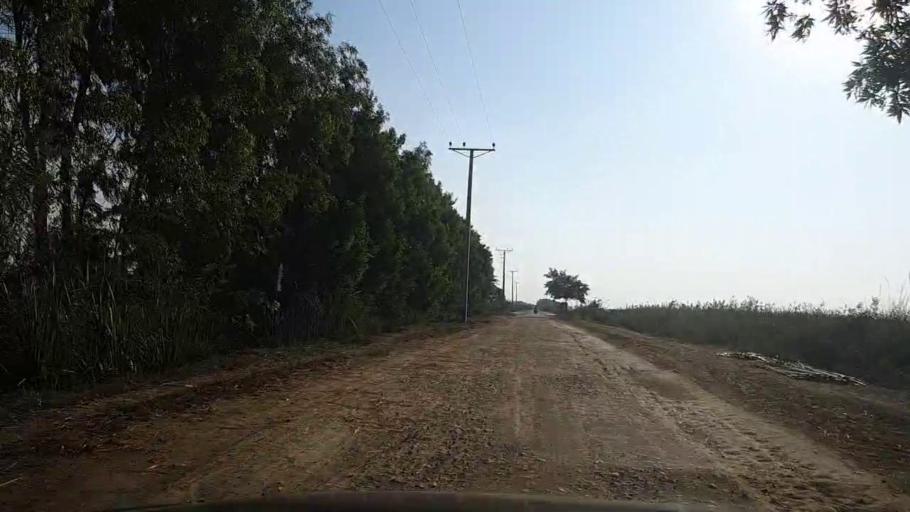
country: PK
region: Sindh
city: Gharo
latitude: 24.7180
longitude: 67.6887
